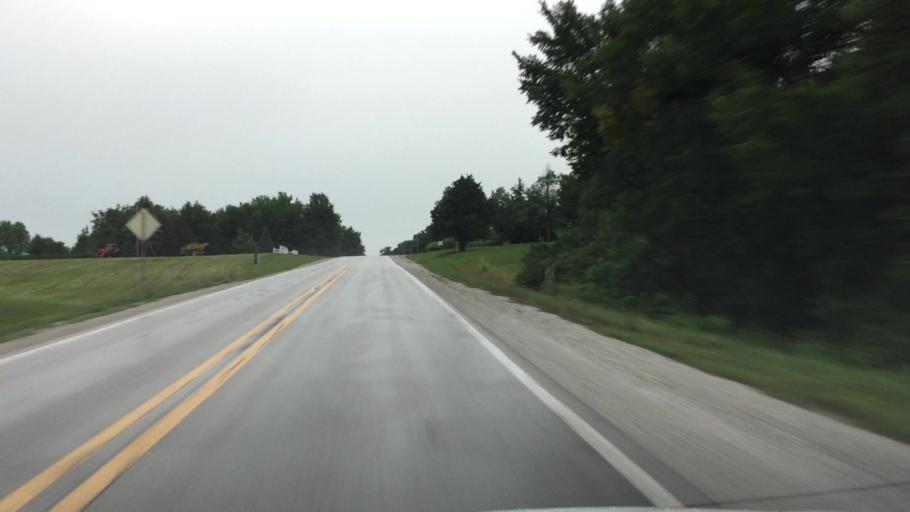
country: US
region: Illinois
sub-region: Hancock County
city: Carthage
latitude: 40.4333
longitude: -91.1401
